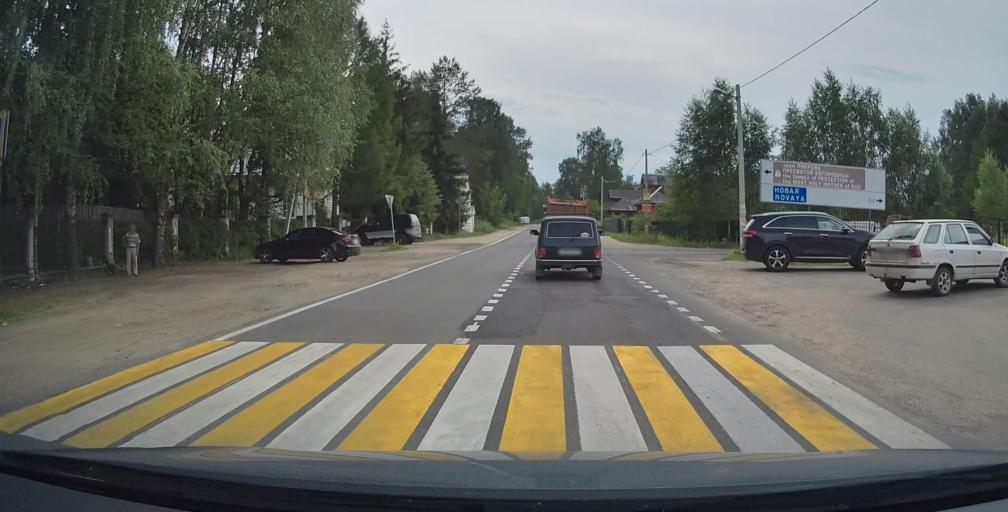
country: RU
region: Jaroslavl
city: Rybinsk
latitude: 57.9993
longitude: 38.7566
